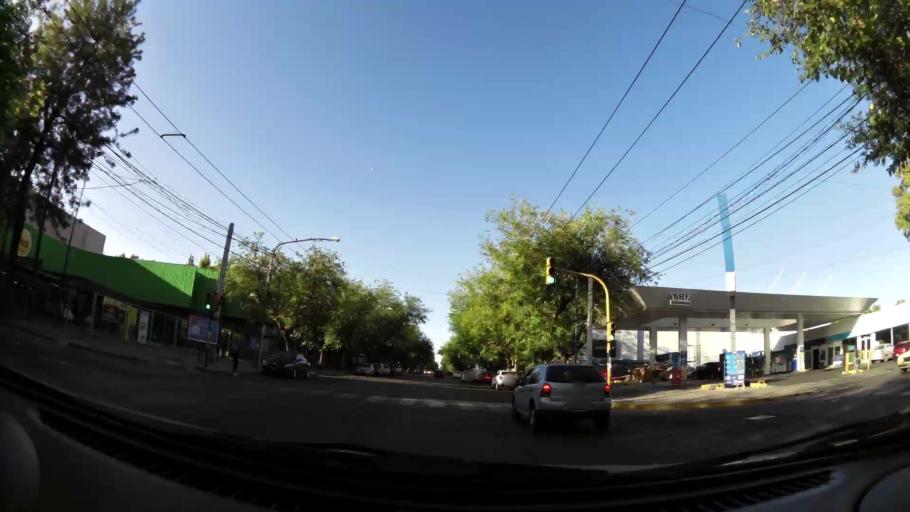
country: AR
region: Mendoza
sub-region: Departamento de Godoy Cruz
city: Godoy Cruz
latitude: -32.9173
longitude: -68.8465
